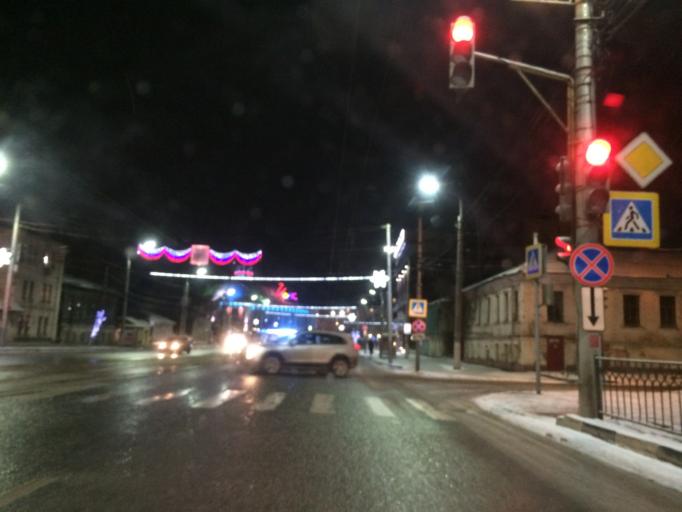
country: RU
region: Tula
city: Tula
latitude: 54.1918
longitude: 37.6279
